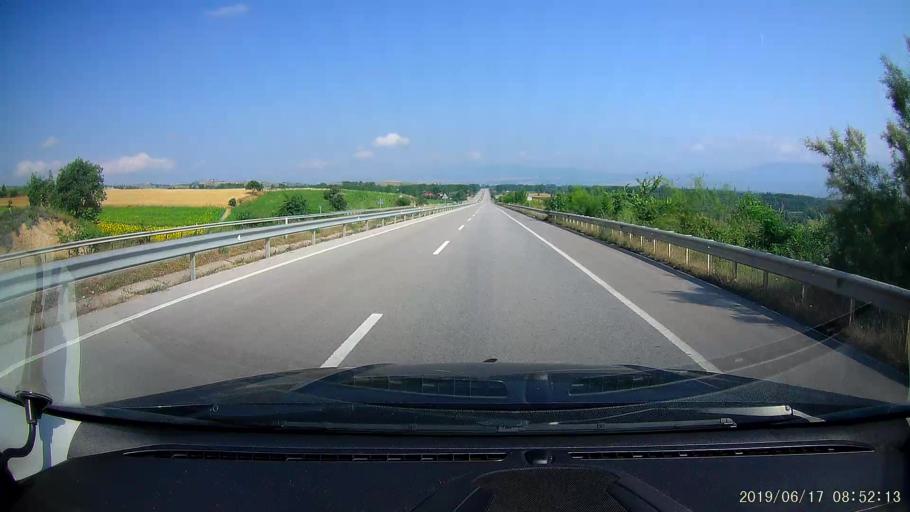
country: TR
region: Tokat
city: Erbaa
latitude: 40.6946
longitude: 36.5004
